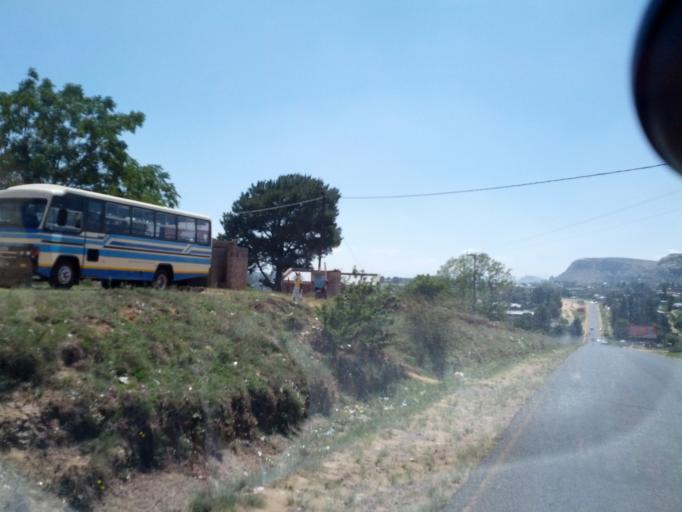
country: LS
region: Butha-Buthe
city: Butha-Buthe
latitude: -28.7748
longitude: 28.2367
